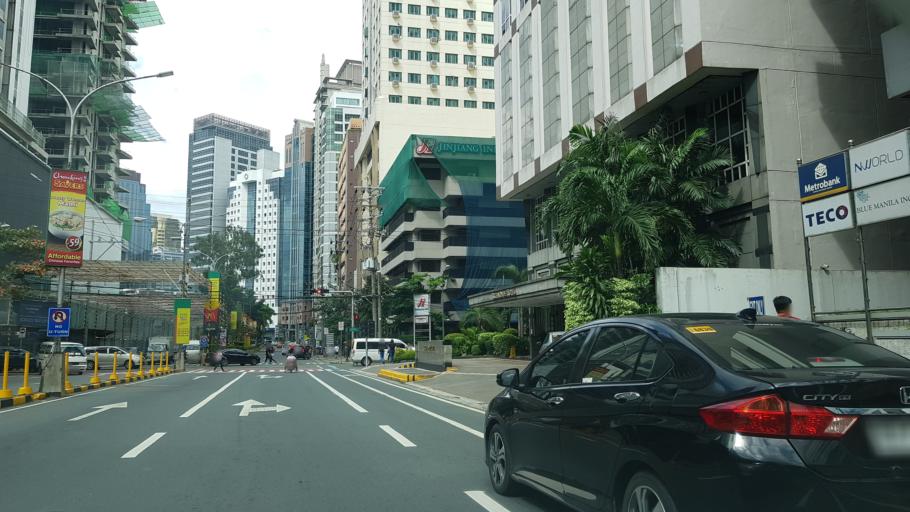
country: PH
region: Metro Manila
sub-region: Pasig
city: Pasig City
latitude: 14.5797
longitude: 121.0585
